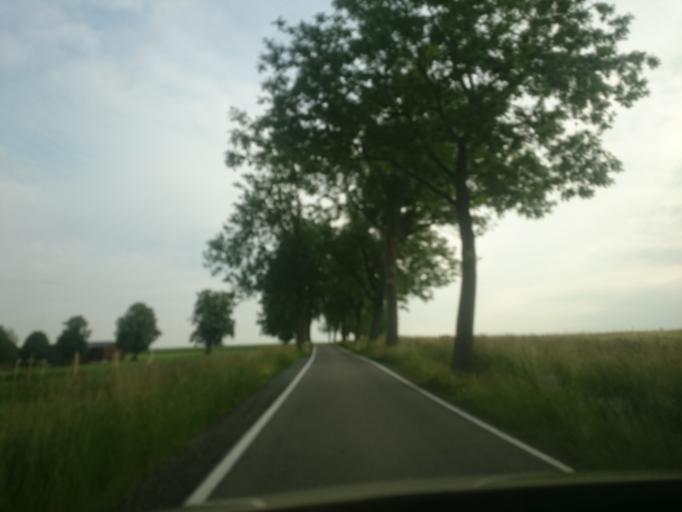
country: DE
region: Saxony
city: Eppendorf
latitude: 50.8462
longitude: 13.2345
